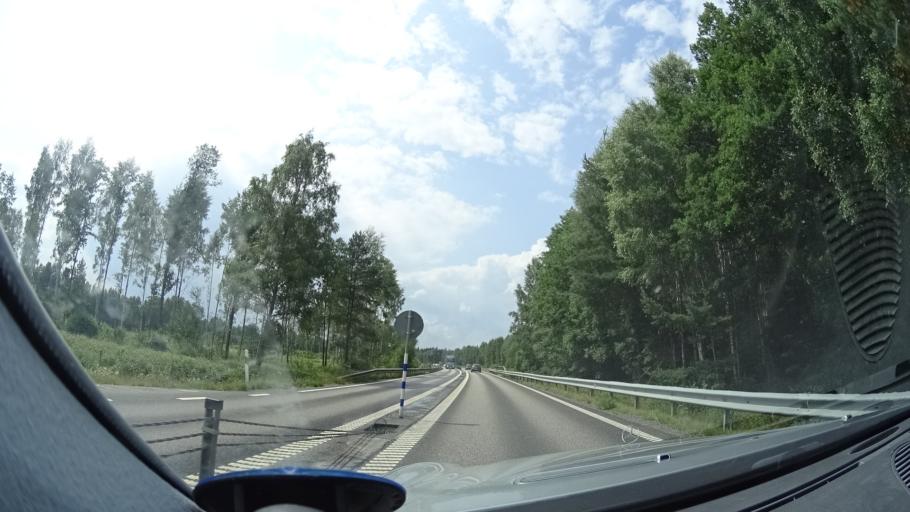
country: SE
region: Kalmar
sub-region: Nybro Kommun
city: Nybro
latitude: 56.7336
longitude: 15.8478
